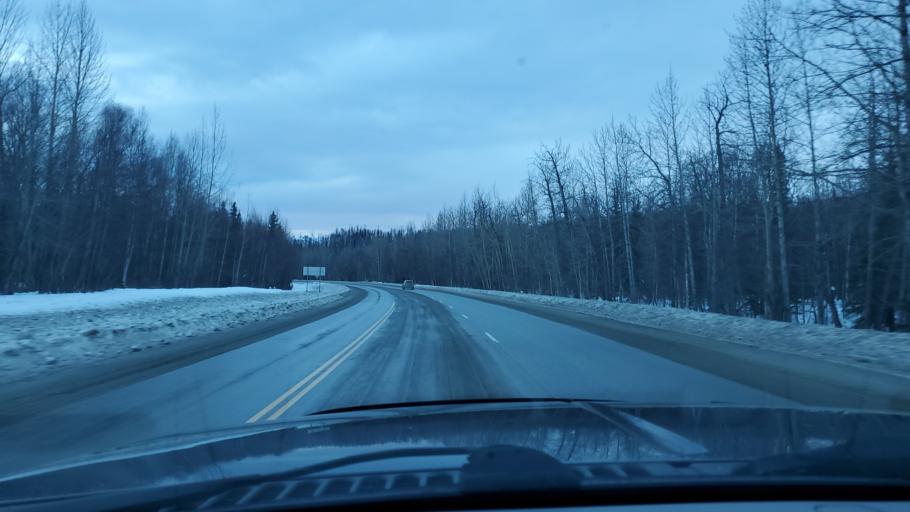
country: US
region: Alaska
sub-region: Matanuska-Susitna Borough
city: Lazy Mountain
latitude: 61.7087
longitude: -148.9374
